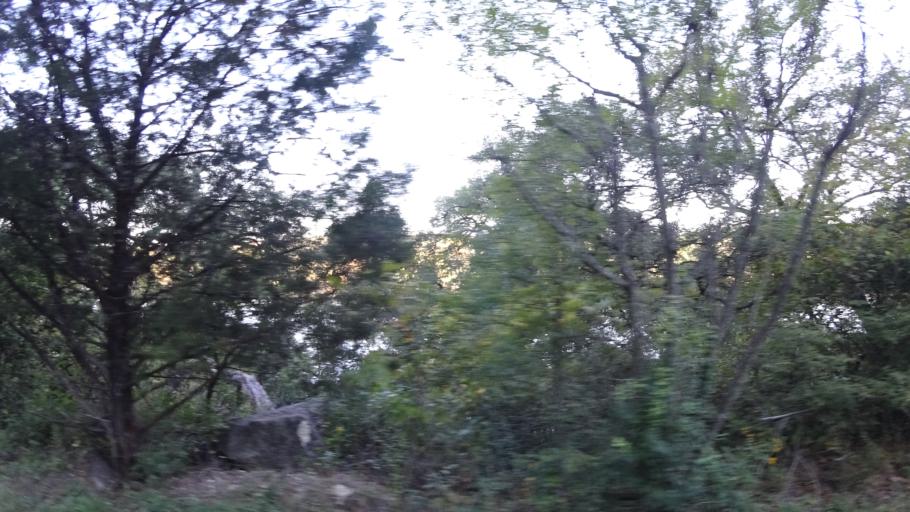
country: US
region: Texas
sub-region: Travis County
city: West Lake Hills
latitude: 30.3460
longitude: -97.8099
